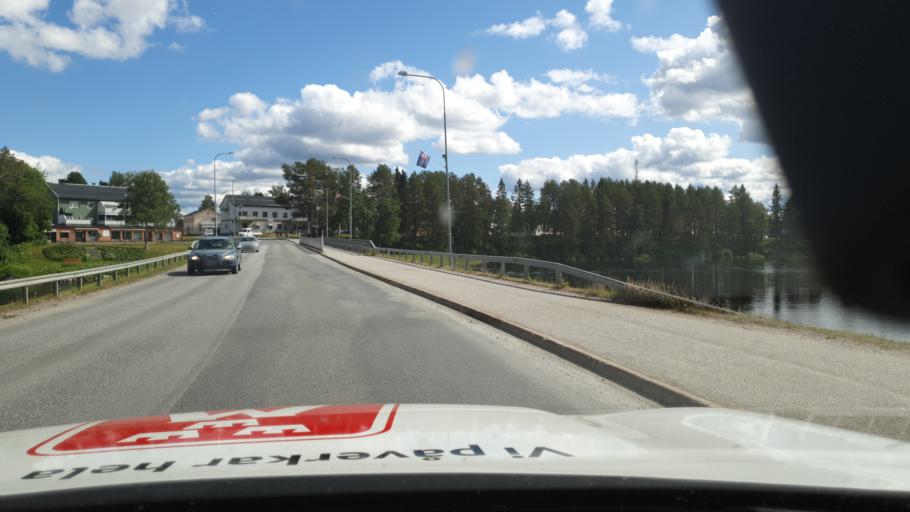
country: SE
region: Vaesterbotten
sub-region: Sorsele Kommun
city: Sorsele
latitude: 65.5354
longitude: 17.5333
